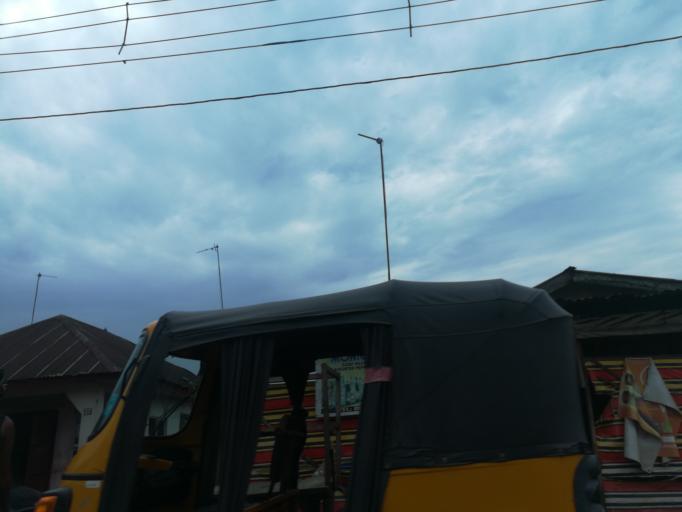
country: NG
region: Rivers
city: Port Harcourt
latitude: 4.8154
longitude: 6.9563
